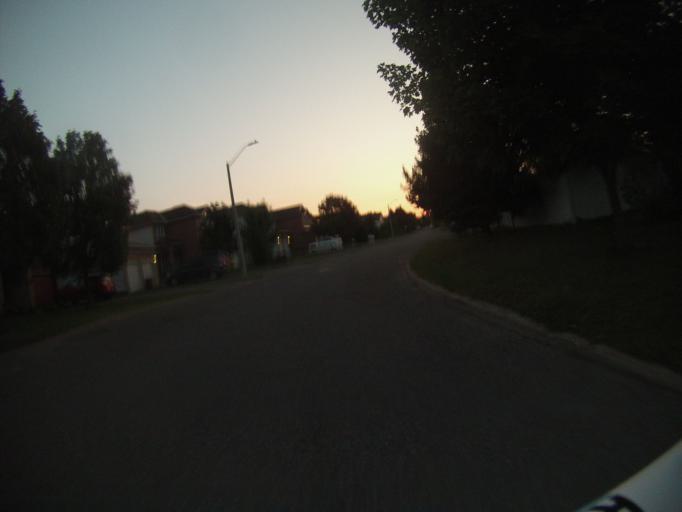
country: CA
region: Ontario
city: Ottawa
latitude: 45.3662
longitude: -75.6316
